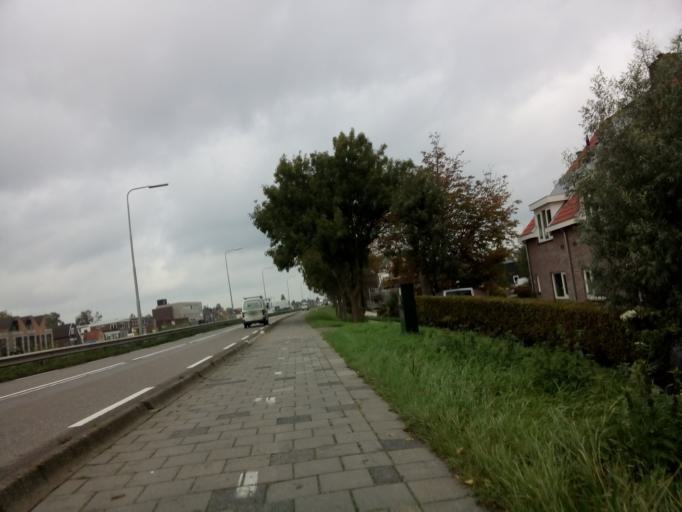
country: NL
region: South Holland
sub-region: Gemeente Waddinxveen
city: Waddinxveen
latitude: 52.0322
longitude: 4.6600
